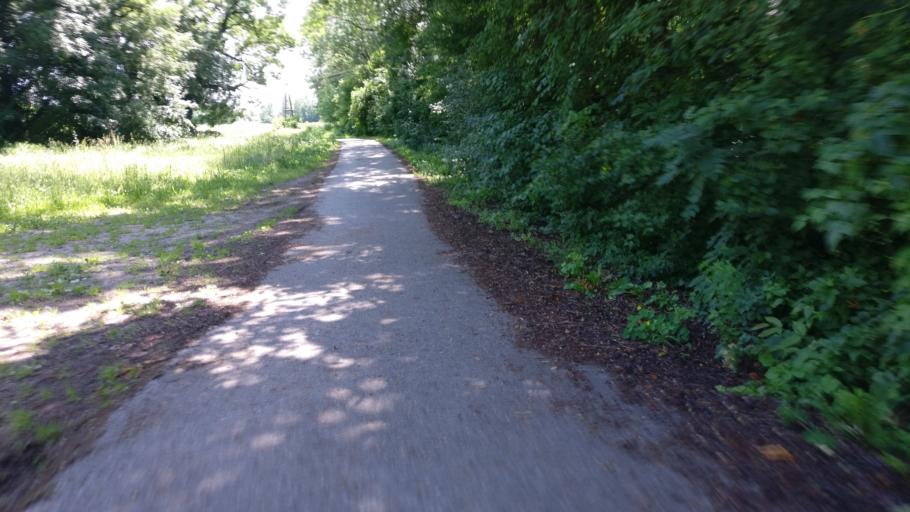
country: AT
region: Lower Austria
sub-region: Politischer Bezirk Wiener Neustadt
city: Sollenau
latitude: 47.9074
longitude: 16.2657
